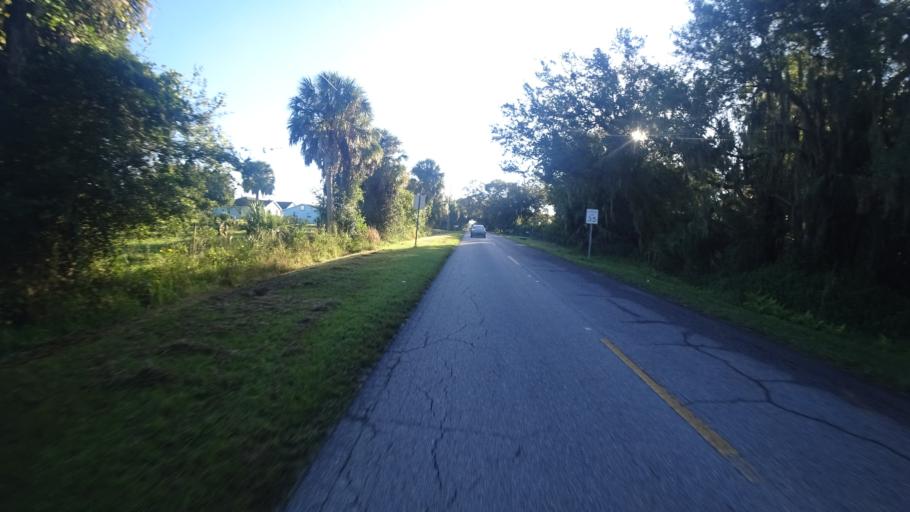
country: US
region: Florida
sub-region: Manatee County
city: Ellenton
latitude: 27.5470
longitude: -82.5348
